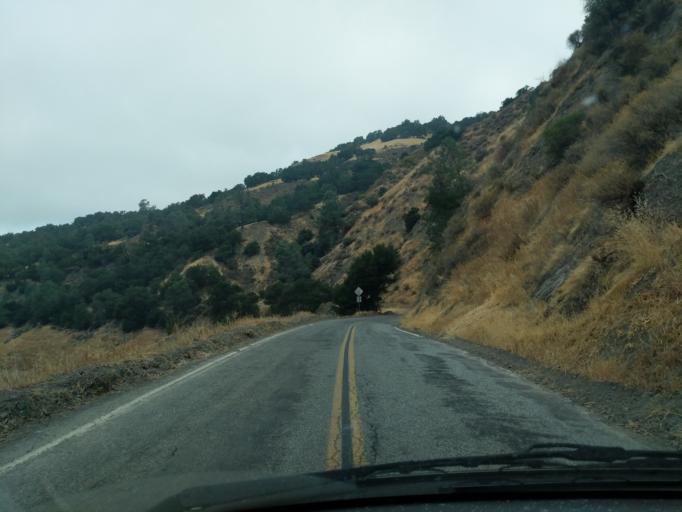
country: US
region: California
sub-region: Santa Clara County
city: San Martin
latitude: 37.1544
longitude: -121.5823
